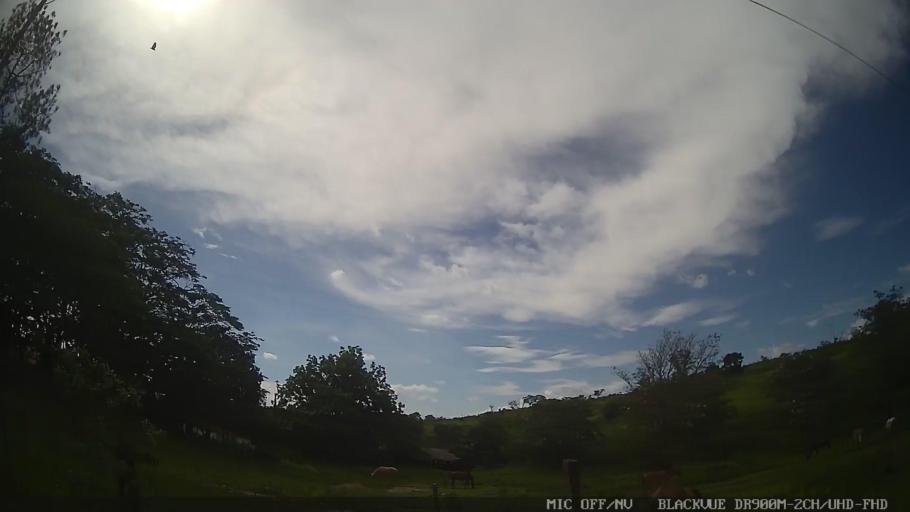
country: BR
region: Sao Paulo
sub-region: Conchas
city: Conchas
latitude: -23.0022
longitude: -48.0011
